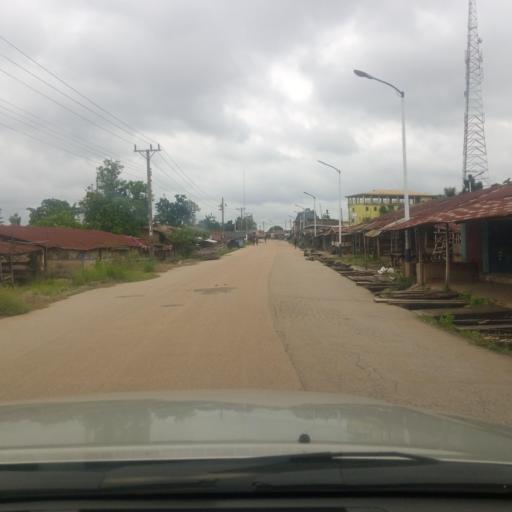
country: NG
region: Ebonyi
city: Effium
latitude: 6.6298
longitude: 8.0556
